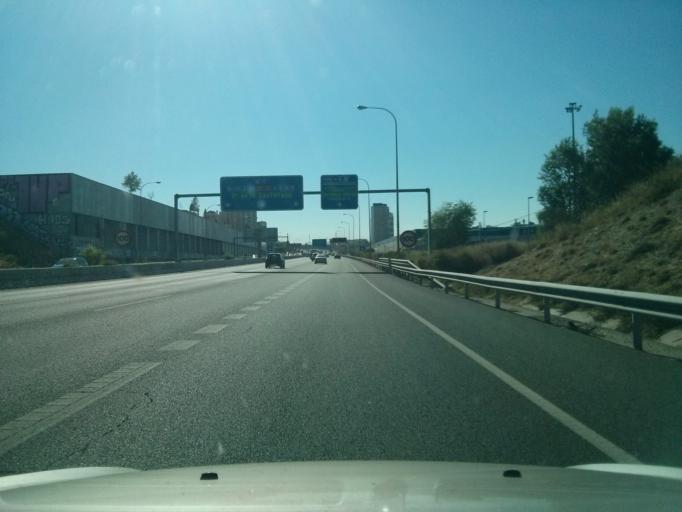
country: ES
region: Madrid
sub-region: Provincia de Madrid
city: Pinar de Chamartin
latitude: 40.4823
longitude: -3.6548
